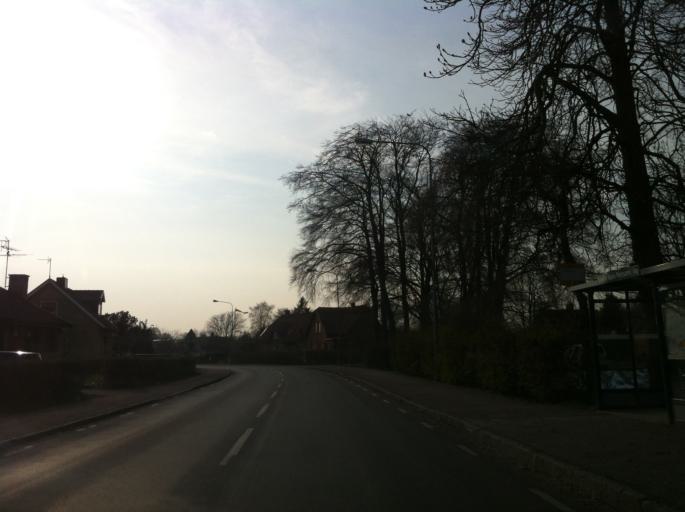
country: SE
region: Skane
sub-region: Svalovs Kommun
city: Svaloev
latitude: 55.9152
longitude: 13.1600
